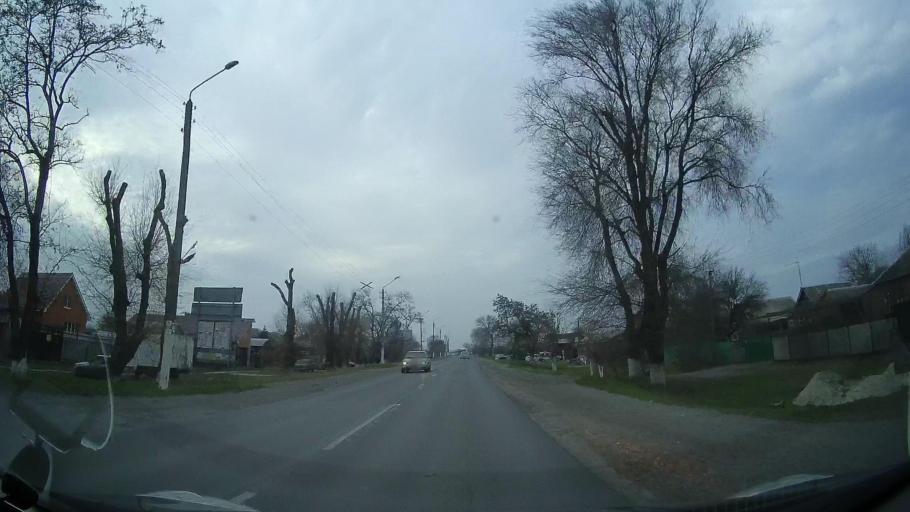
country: RU
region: Rostov
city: Ol'ginskaya
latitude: 47.1960
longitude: 39.9399
